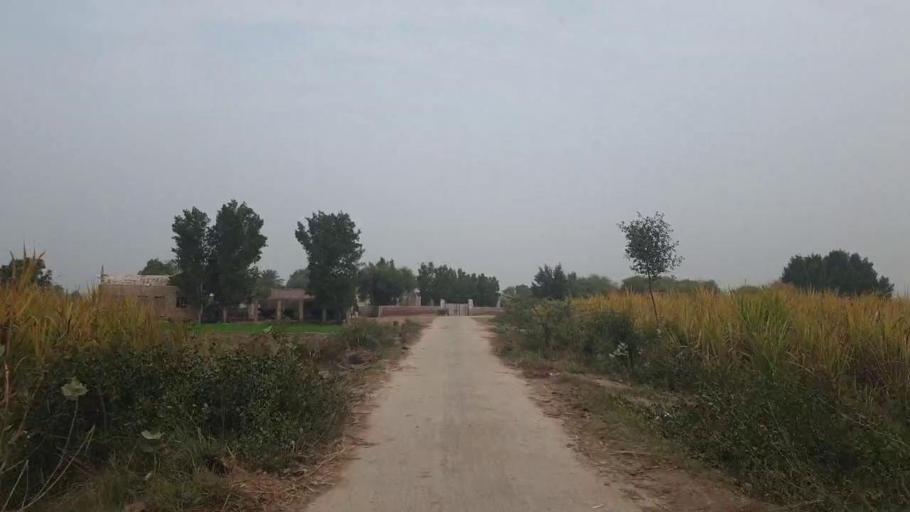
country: PK
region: Sindh
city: Tando Adam
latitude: 25.7746
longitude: 68.6834
